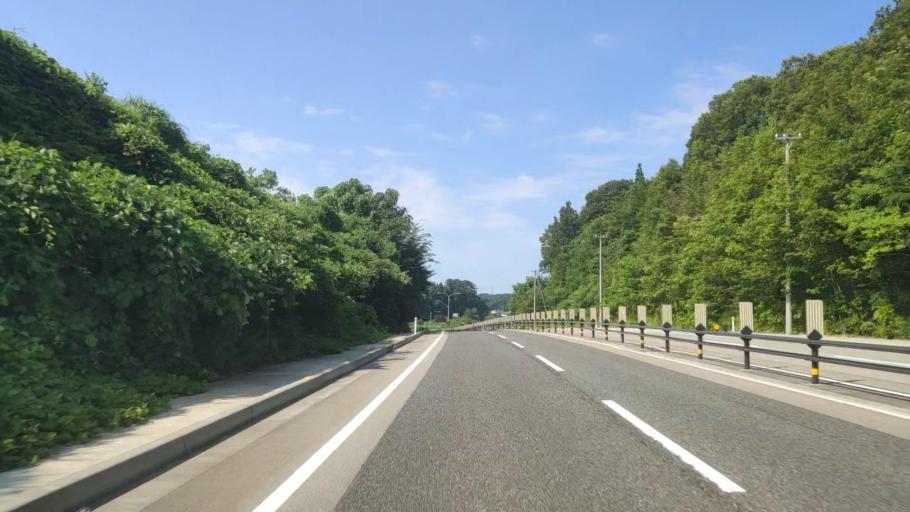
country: JP
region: Ishikawa
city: Komatsu
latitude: 36.4280
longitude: 136.5325
